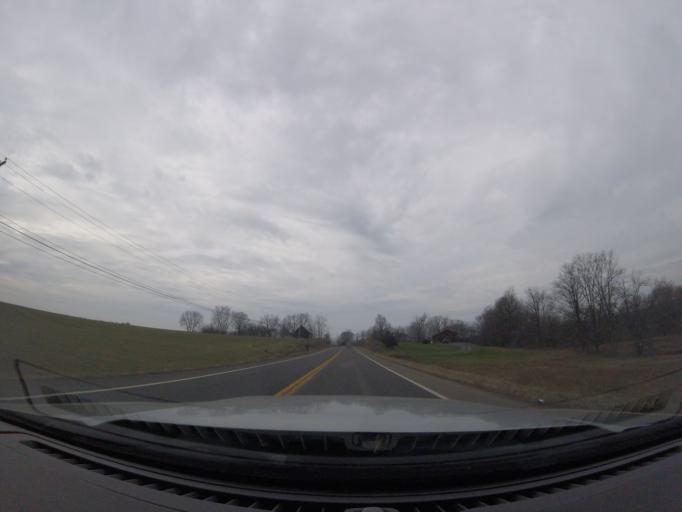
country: US
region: New York
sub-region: Schuyler County
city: Watkins Glen
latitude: 42.4238
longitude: -76.8262
